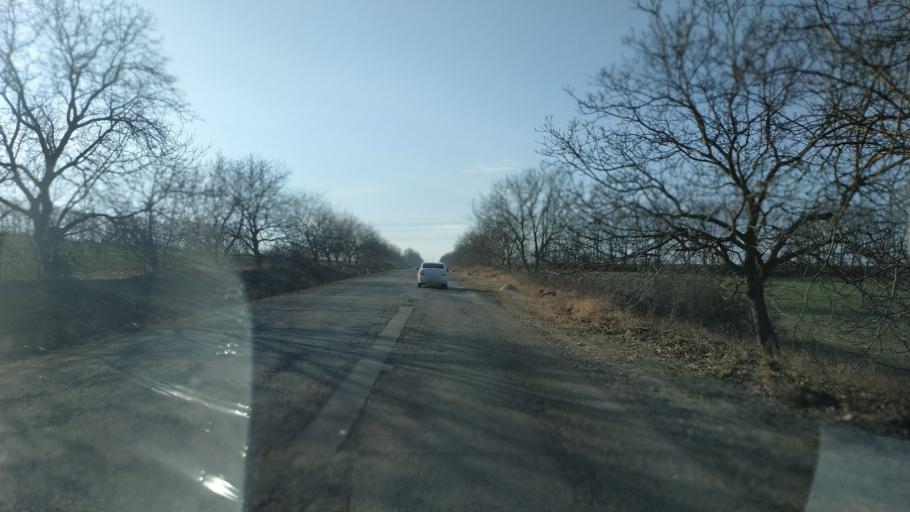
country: MD
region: Chisinau
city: Singera
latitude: 46.8759
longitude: 29.0396
